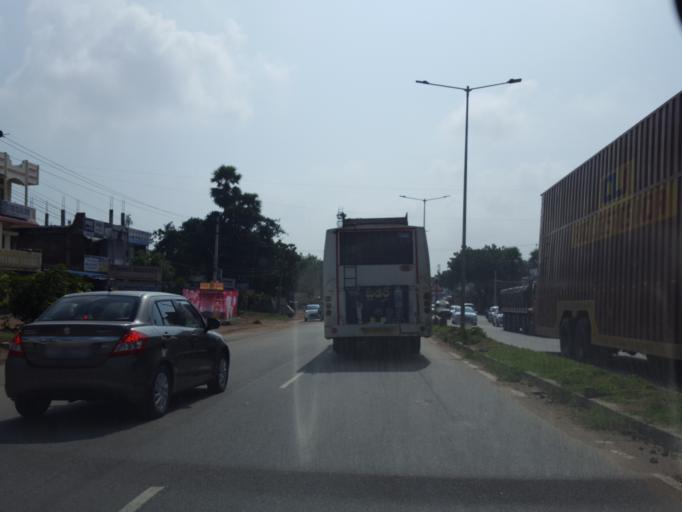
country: IN
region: Telangana
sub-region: Rangareddi
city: Lal Bahadur Nagar
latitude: 17.3112
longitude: 78.6838
